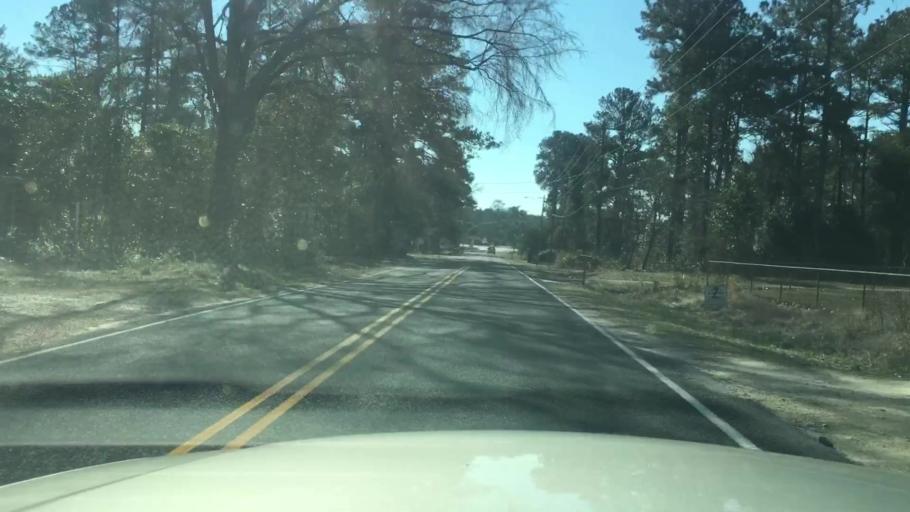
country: US
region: North Carolina
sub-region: Cumberland County
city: Hope Mills
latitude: 34.9973
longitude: -78.9652
